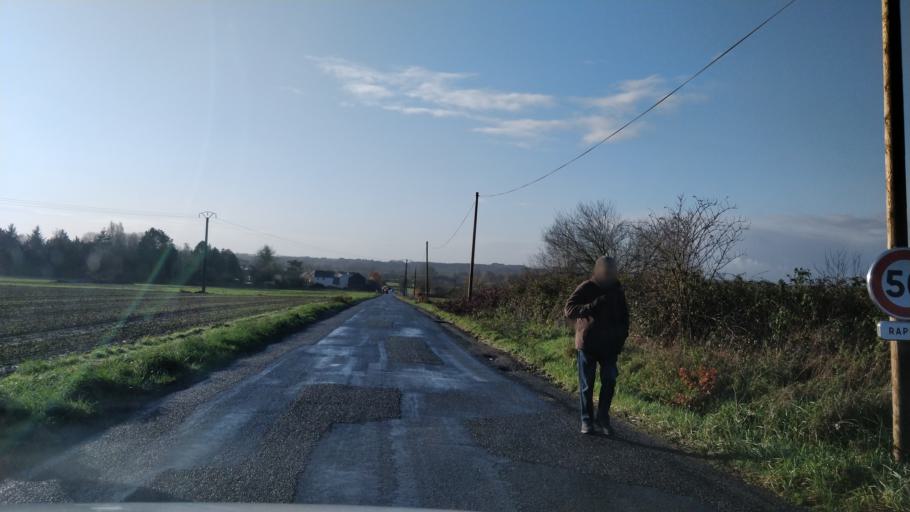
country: FR
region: Brittany
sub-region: Departement d'Ille-et-Vilaine
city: Chavagne
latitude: 48.0573
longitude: -1.7996
